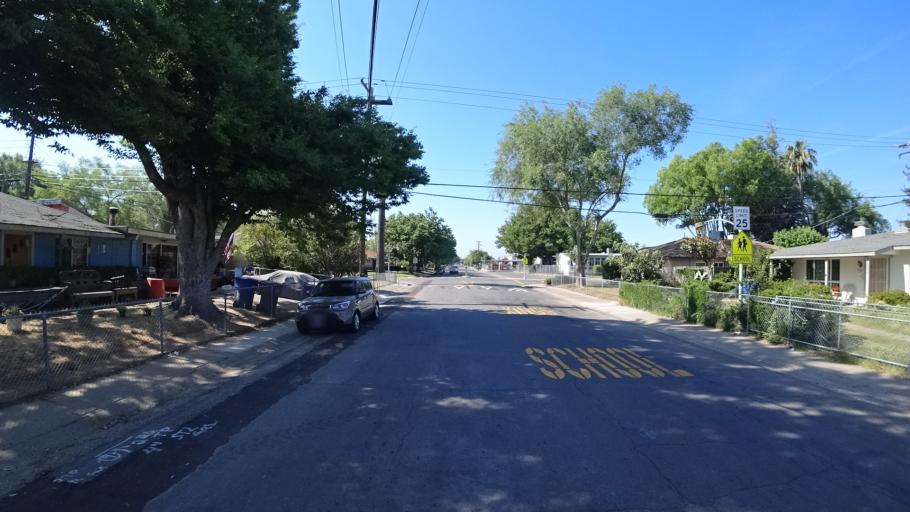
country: US
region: California
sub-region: Sacramento County
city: Parkway
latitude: 38.5316
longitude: -121.4387
